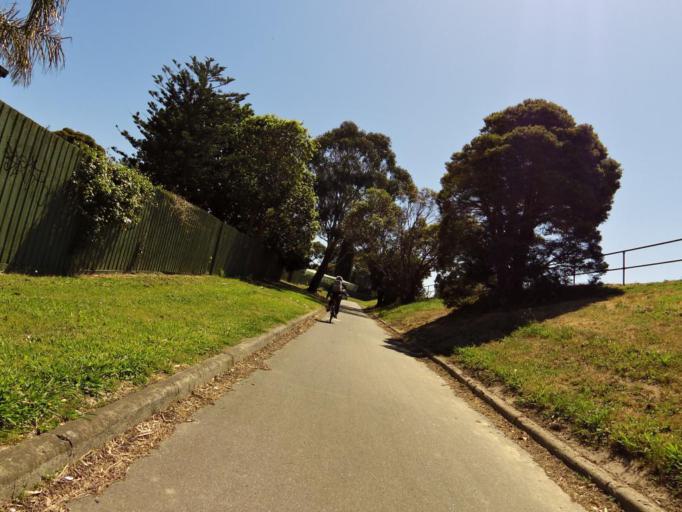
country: AU
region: Victoria
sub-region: Knox
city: Knoxfield
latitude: -37.8662
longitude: 145.2420
